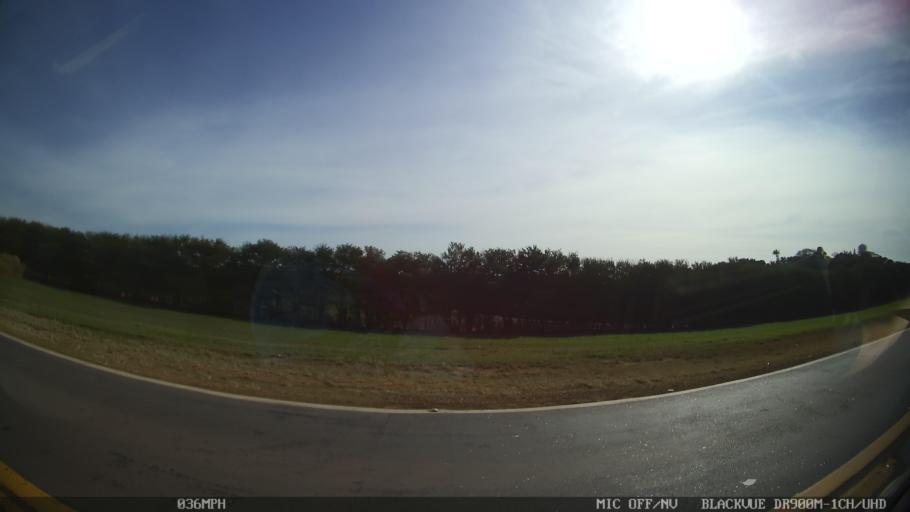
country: BR
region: Sao Paulo
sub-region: Rio Das Pedras
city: Rio das Pedras
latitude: -22.7957
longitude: -47.5948
